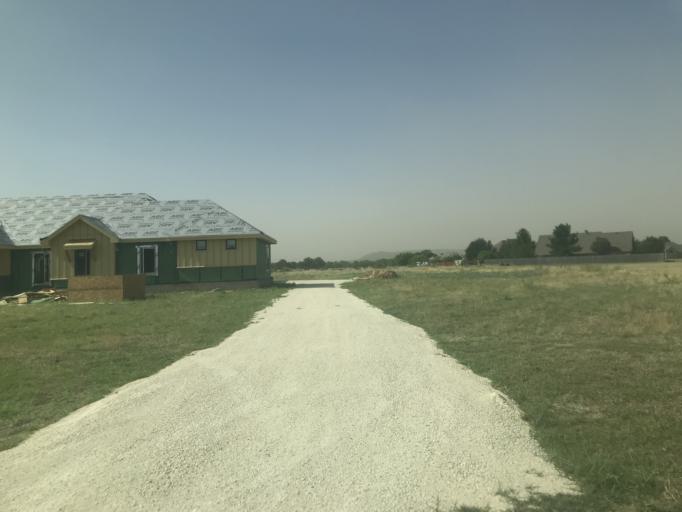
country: US
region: Texas
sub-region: Taylor County
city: Potosi
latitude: 32.3403
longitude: -99.7097
